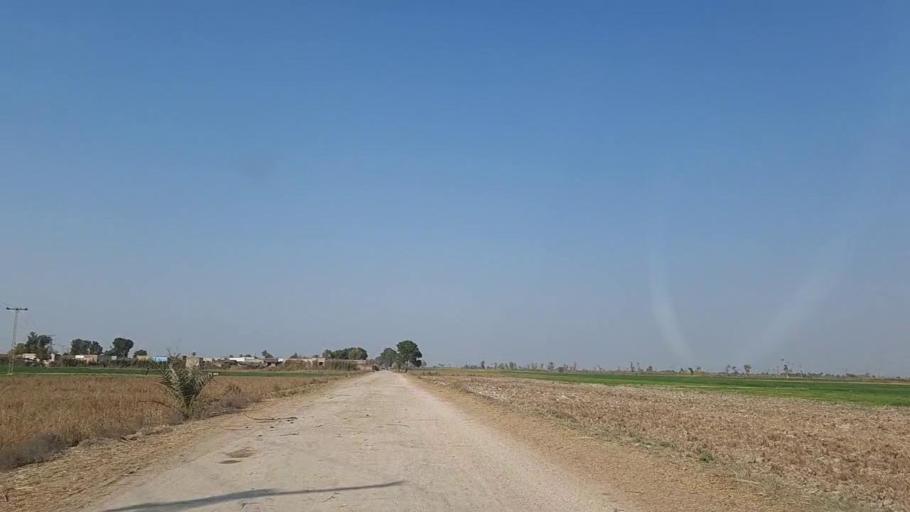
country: PK
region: Sindh
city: Daur
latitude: 26.4761
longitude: 68.2971
